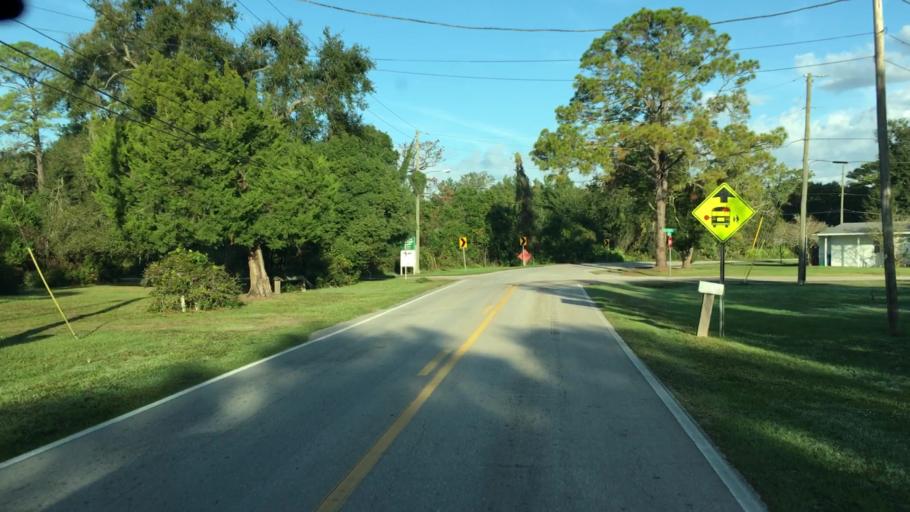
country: US
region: Florida
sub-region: Volusia County
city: North DeLand
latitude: 29.0658
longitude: -81.2707
